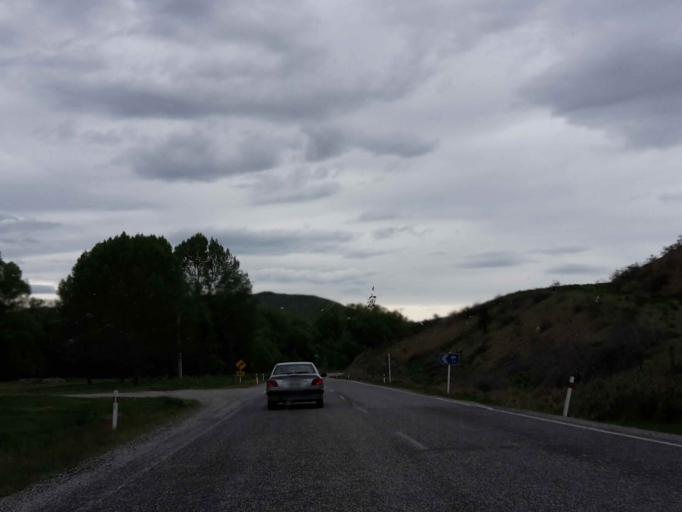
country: NZ
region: Otago
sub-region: Queenstown-Lakes District
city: Wanaka
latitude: -44.7179
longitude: 169.5054
